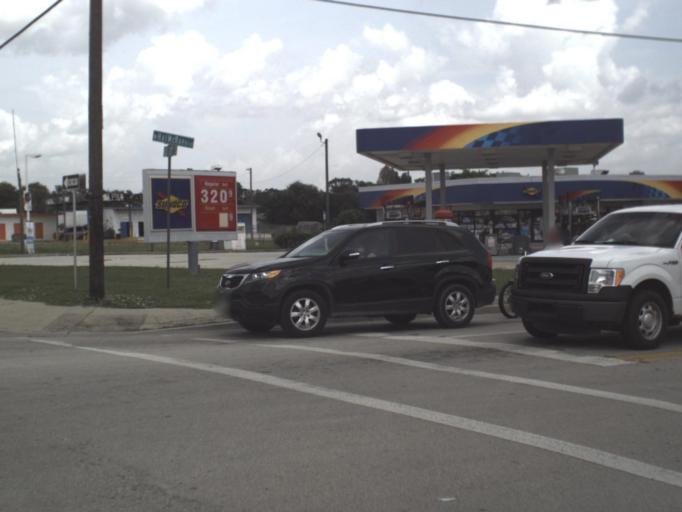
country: US
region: Florida
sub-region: Highlands County
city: Avon Park
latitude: 27.5846
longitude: -81.5144
